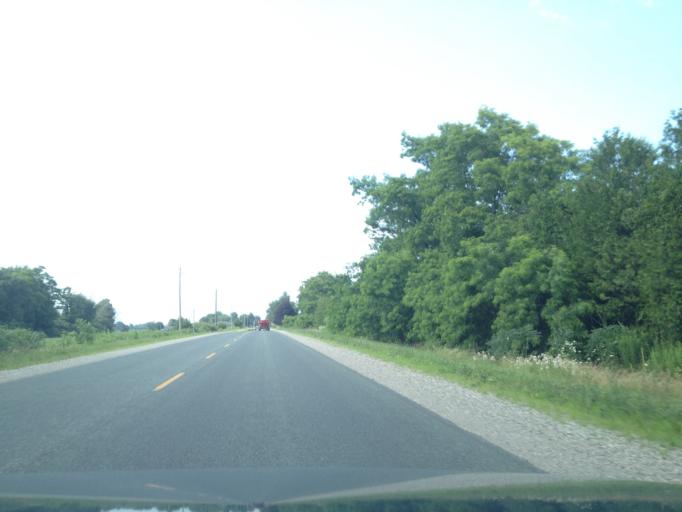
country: CA
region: Ontario
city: Aylmer
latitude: 42.7024
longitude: -80.8593
